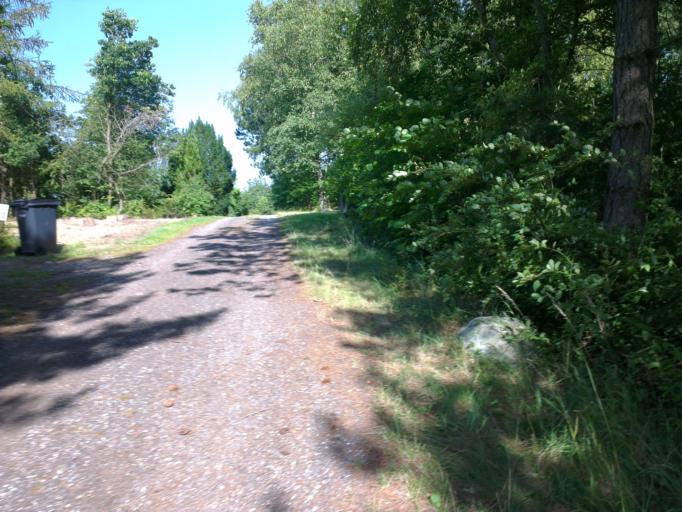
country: DK
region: Capital Region
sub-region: Halsnaes Kommune
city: Hundested
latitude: 55.9248
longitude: 11.9313
